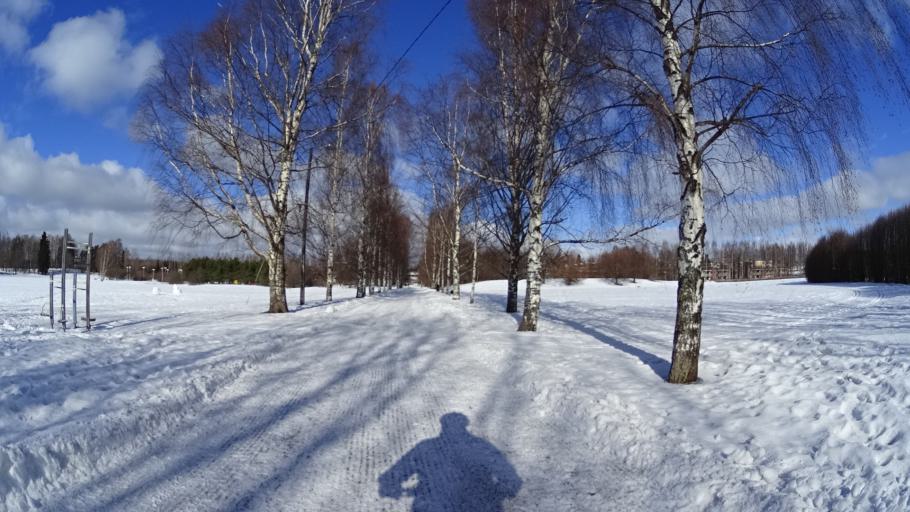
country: FI
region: Uusimaa
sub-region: Helsinki
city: Teekkarikylae
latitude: 60.2406
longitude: 24.8650
